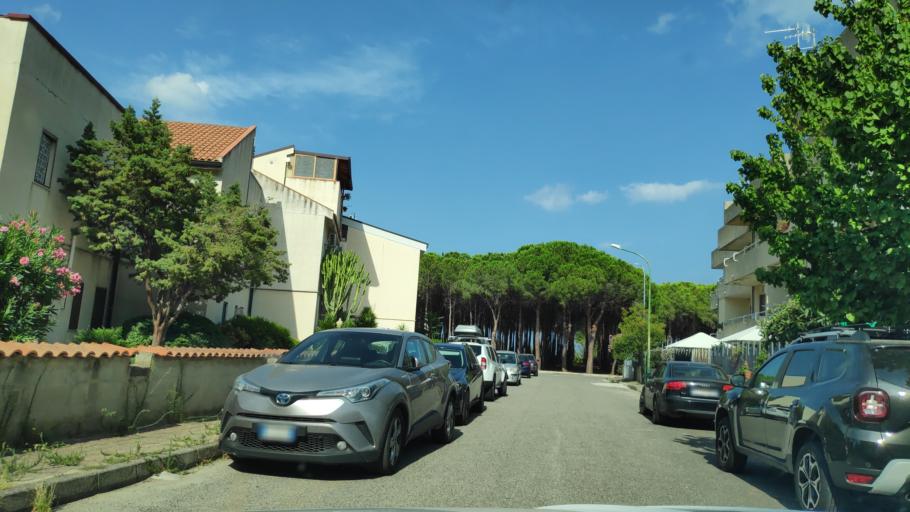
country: IT
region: Calabria
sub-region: Provincia di Catanzaro
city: Soverato Marina
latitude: 38.6819
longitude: 16.5551
